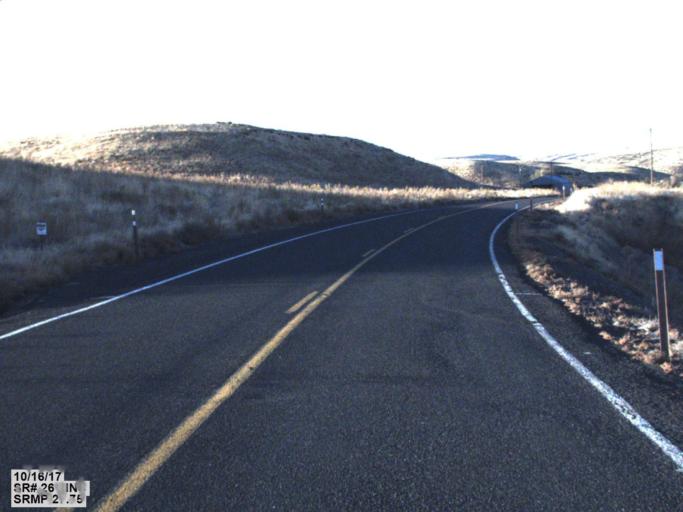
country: US
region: Washington
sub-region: Adams County
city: Ritzville
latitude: 46.6896
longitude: -118.3892
